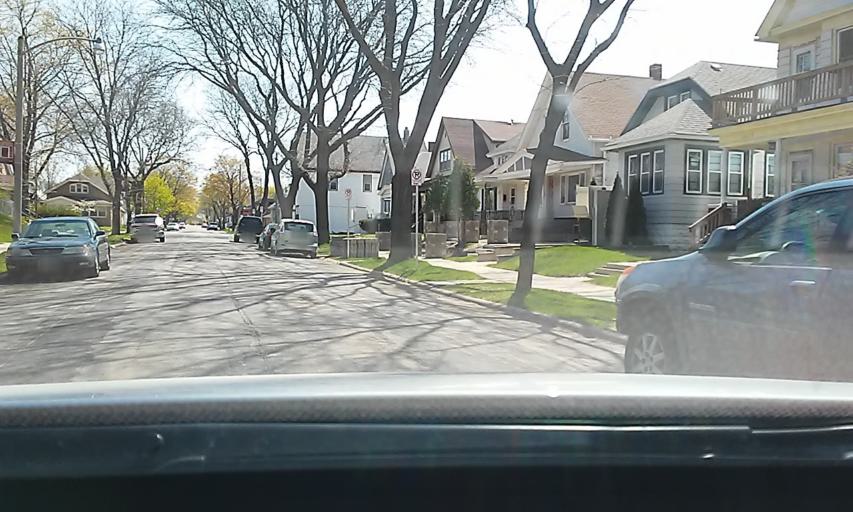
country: US
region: Wisconsin
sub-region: Milwaukee County
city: West Milwaukee
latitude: 43.0048
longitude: -87.9566
